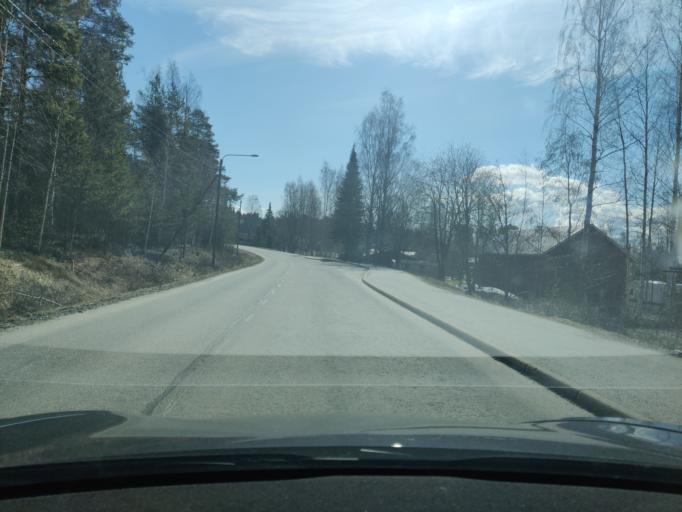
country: FI
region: Northern Savo
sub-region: Kuopio
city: Vehmersalmi
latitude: 62.7660
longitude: 28.0179
